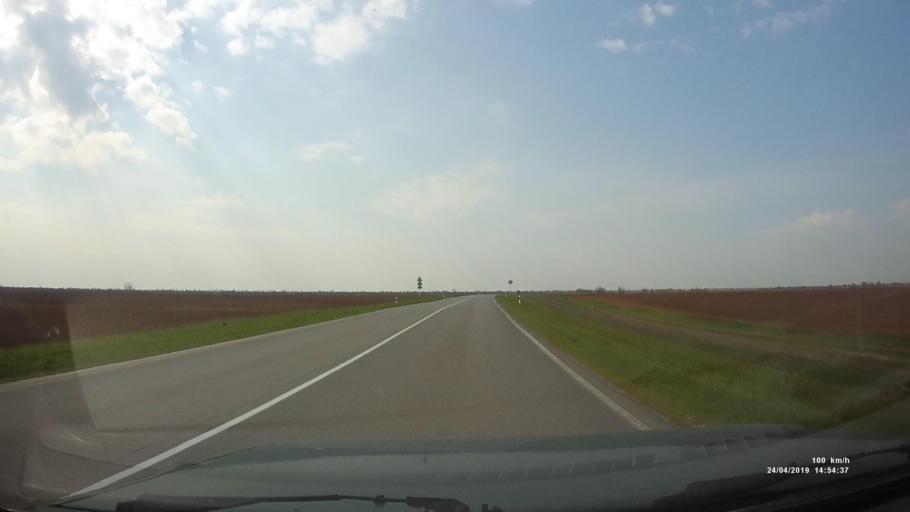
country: RU
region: Rostov
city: Remontnoye
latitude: 46.5356
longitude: 43.6358
